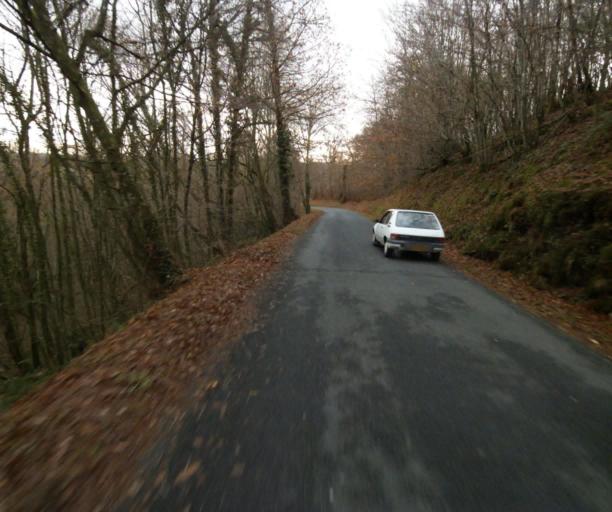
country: FR
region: Limousin
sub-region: Departement de la Correze
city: Chameyrat
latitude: 45.2277
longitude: 1.7028
